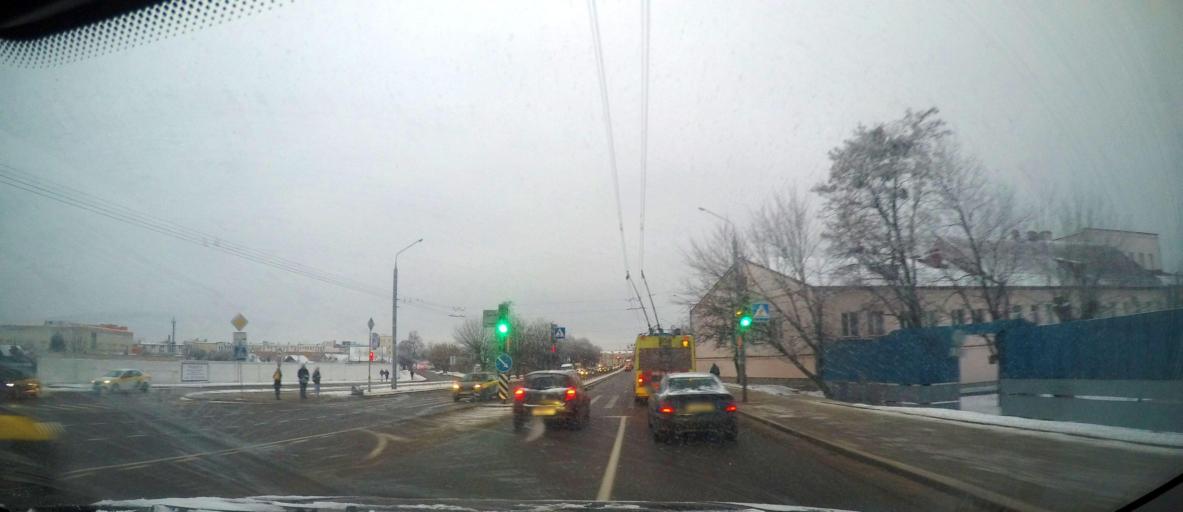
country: BY
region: Grodnenskaya
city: Hrodna
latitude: 53.6660
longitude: 23.8267
